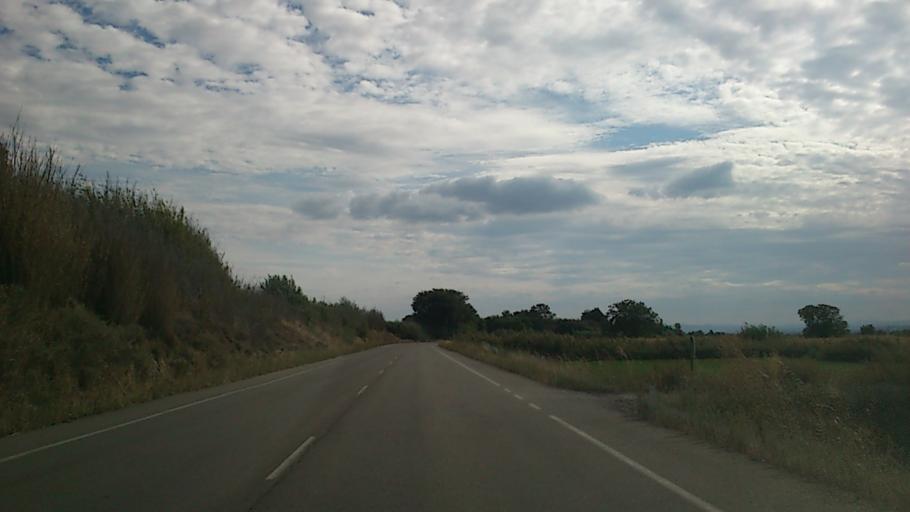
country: ES
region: Aragon
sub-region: Provincia de Zaragoza
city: Villanueva de Gallego
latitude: 41.7756
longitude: -0.7897
